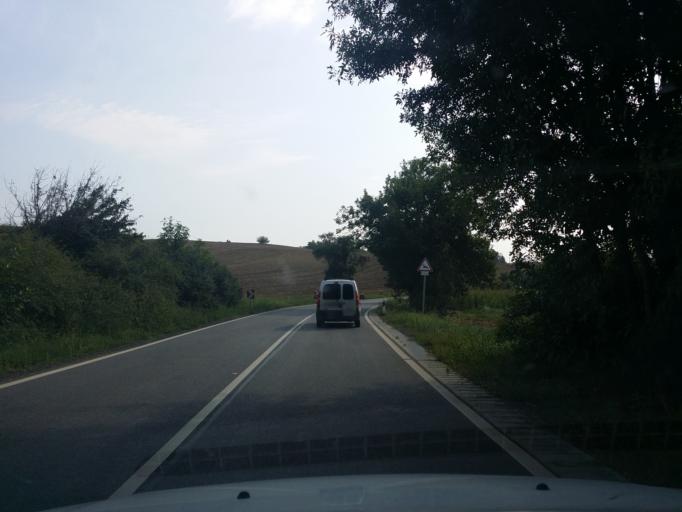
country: HU
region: Pest
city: Acsa
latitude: 47.7943
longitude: 19.3729
